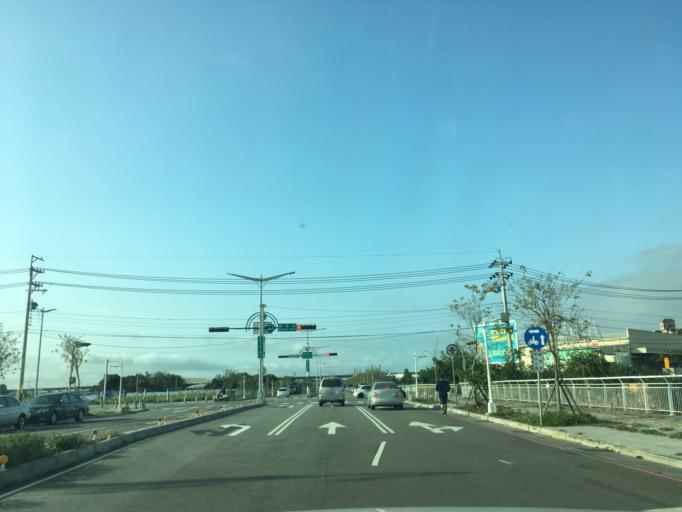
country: TW
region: Taiwan
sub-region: Taichung City
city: Taichung
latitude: 24.1922
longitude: 120.6934
